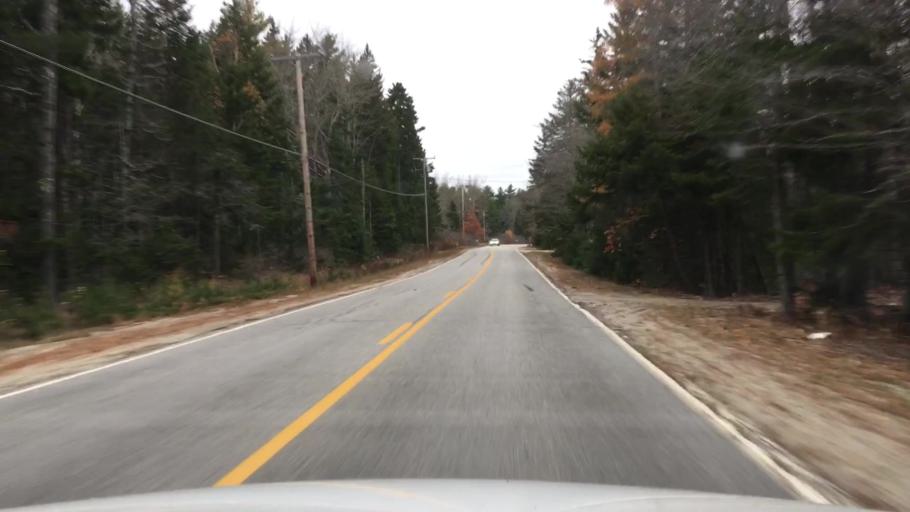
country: US
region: Maine
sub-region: Hancock County
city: Sedgwick
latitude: 44.2864
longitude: -68.5550
